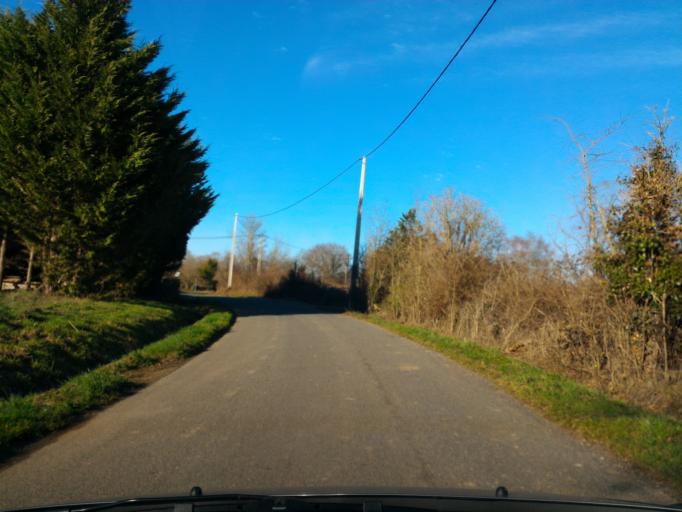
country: FR
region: Poitou-Charentes
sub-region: Departement de la Charente
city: Nanteuil-en-Vallee
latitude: 45.9553
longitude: 0.3559
